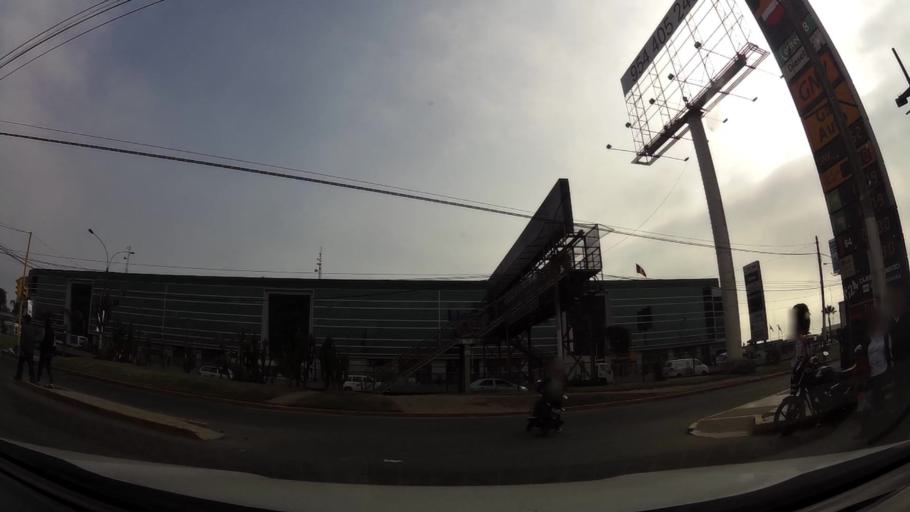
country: PE
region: Callao
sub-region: Callao
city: Callao
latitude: -12.0279
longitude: -77.1026
